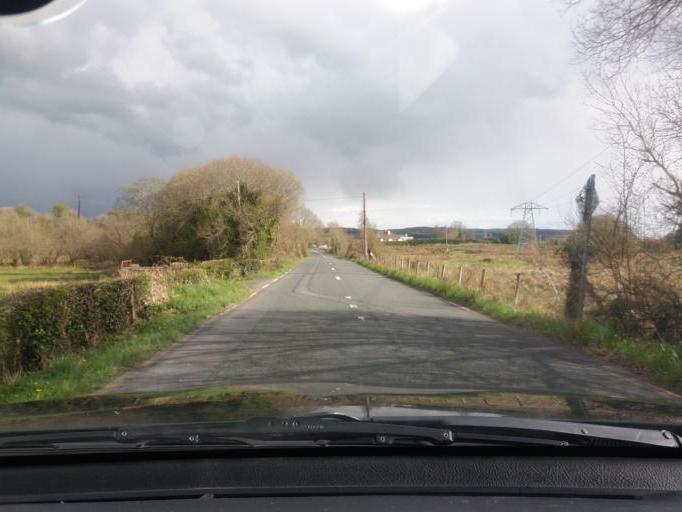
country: IE
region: Connaught
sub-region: County Leitrim
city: Manorhamilton
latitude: 54.3134
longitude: -8.1884
